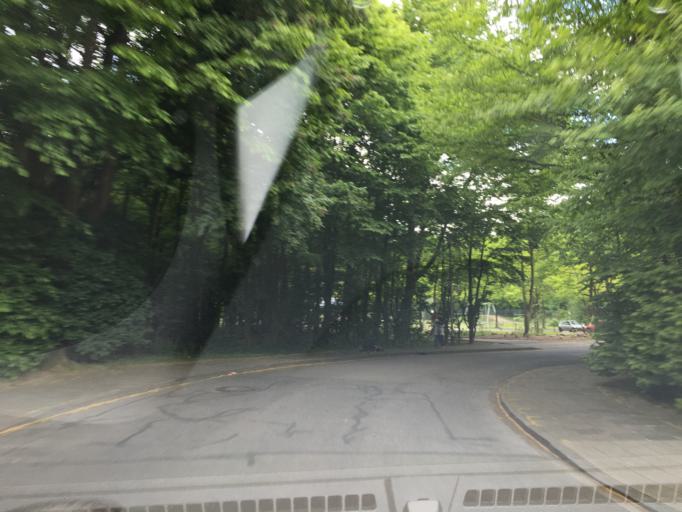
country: DE
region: North Rhine-Westphalia
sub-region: Regierungsbezirk Munster
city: Muenster
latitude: 51.9991
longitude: 7.6400
